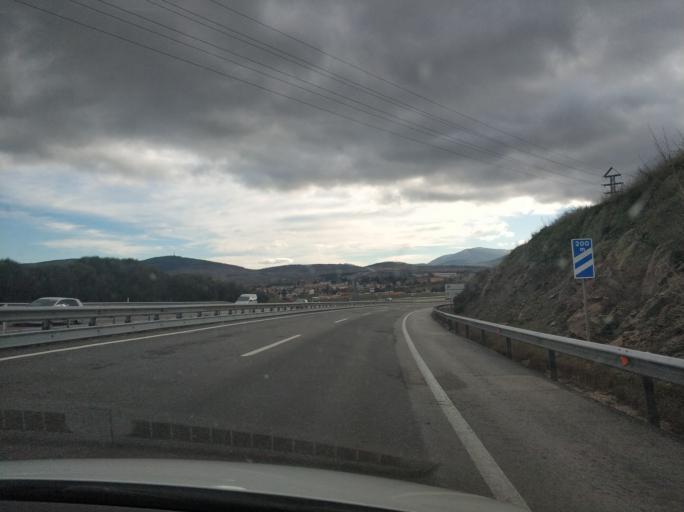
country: ES
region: Madrid
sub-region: Provincia de Madrid
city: Buitrago del Lozoya
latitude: 41.0032
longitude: -3.6376
